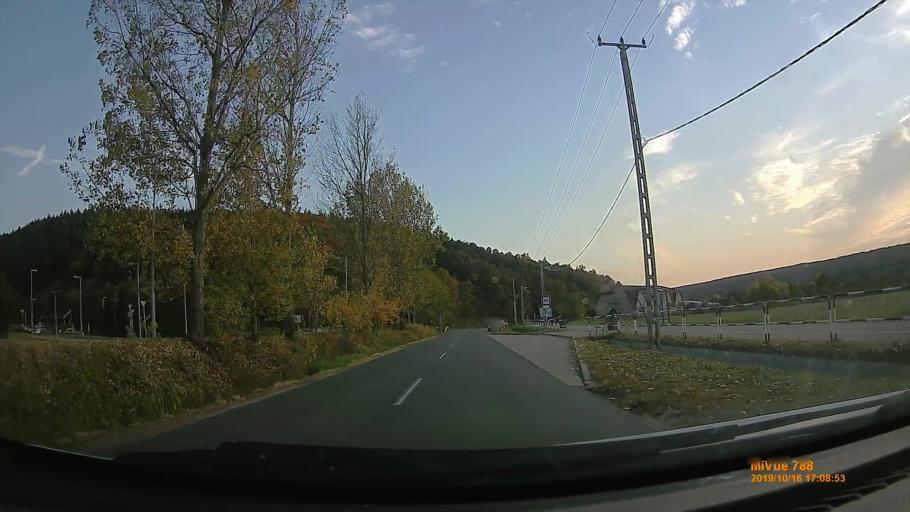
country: HU
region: Heves
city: Egerszalok
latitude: 47.8550
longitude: 20.3294
